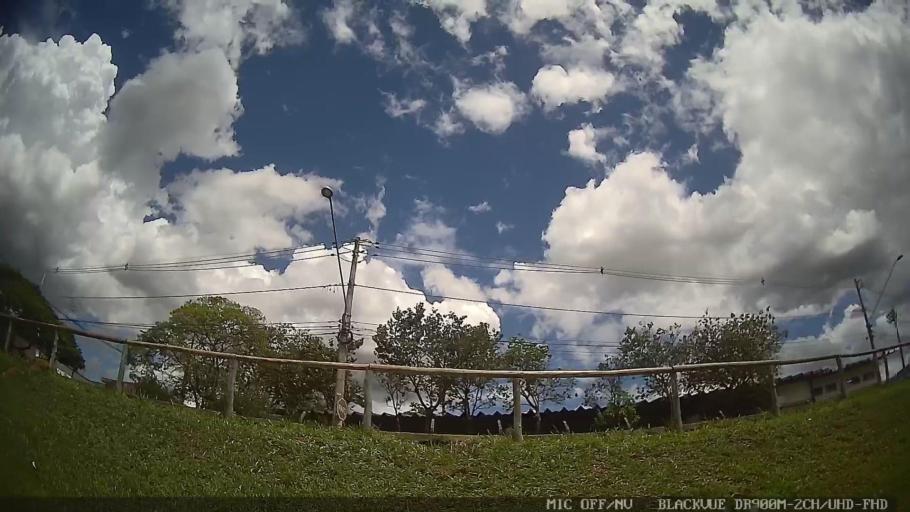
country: BR
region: Sao Paulo
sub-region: Jaguariuna
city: Jaguariuna
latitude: -22.6943
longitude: -46.9911
